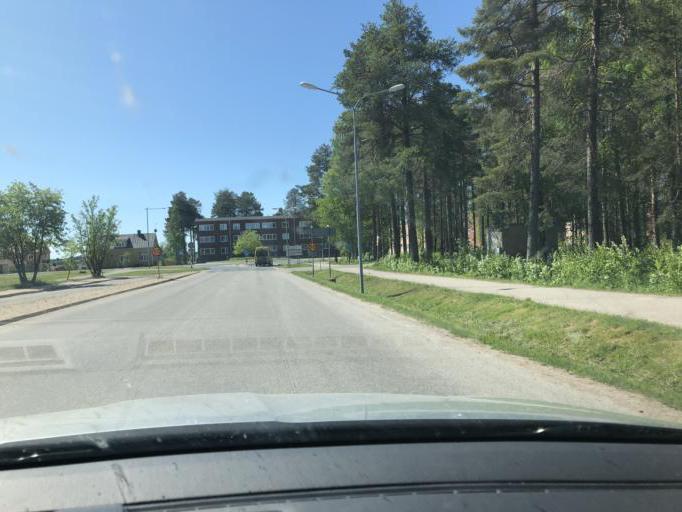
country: SE
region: Norrbotten
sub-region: Kalix Kommun
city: Kalix
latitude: 65.8534
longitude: 23.1599
